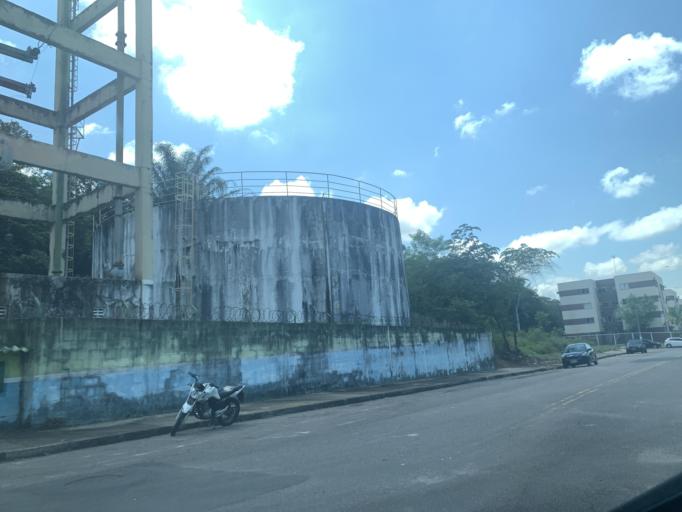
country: BR
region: Amazonas
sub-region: Manaus
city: Manaus
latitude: -3.1066
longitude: -59.9690
